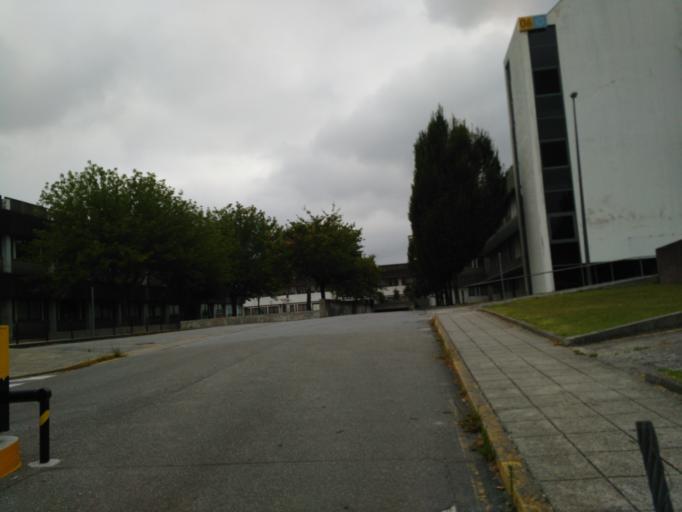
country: PT
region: Braga
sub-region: Braga
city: Adaufe
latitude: 41.5609
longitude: -8.3952
